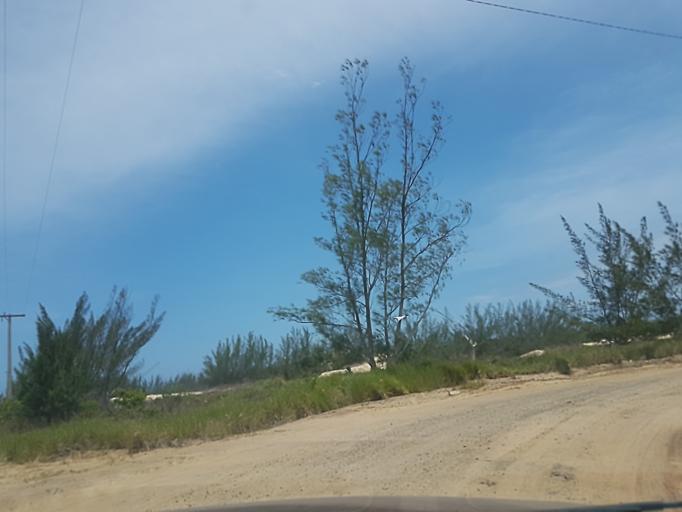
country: BR
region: Santa Catarina
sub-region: Jaguaruna
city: Jaguaruna
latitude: -28.6561
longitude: -48.9550
